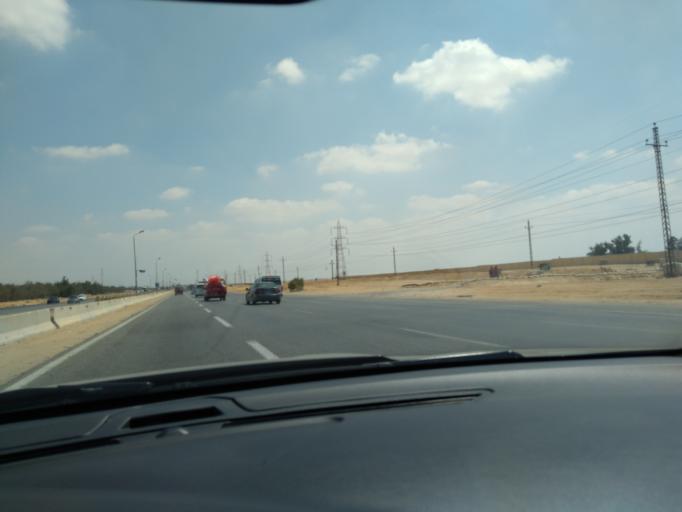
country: EG
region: Al Isma'iliyah
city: At Tall al Kabir
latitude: 30.4009
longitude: 31.9864
